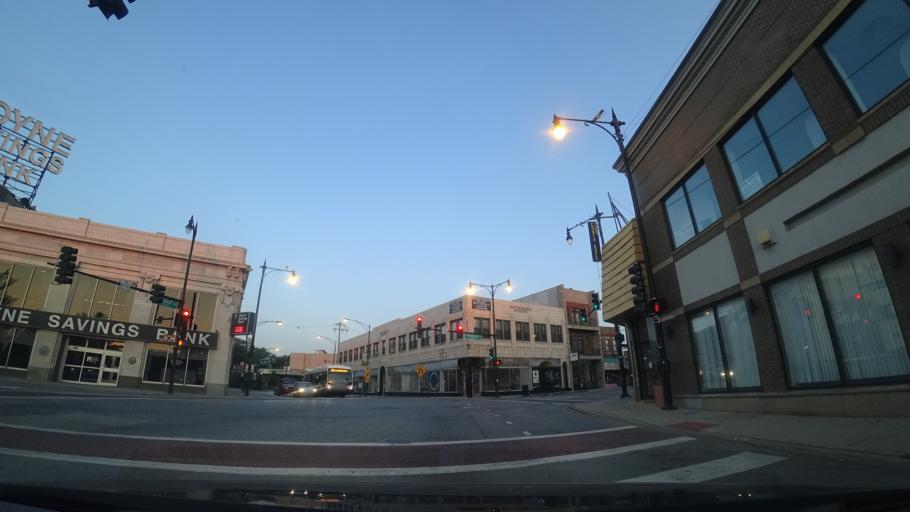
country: US
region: Illinois
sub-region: Cook County
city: Harwood Heights
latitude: 41.9679
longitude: -87.7605
